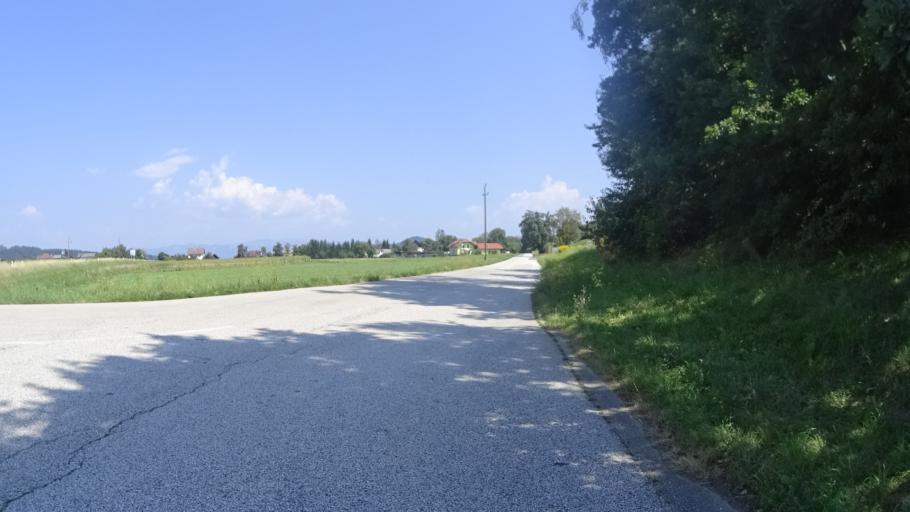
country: AT
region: Carinthia
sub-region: Politischer Bezirk Volkermarkt
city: Eberndorf
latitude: 46.5708
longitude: 14.6313
